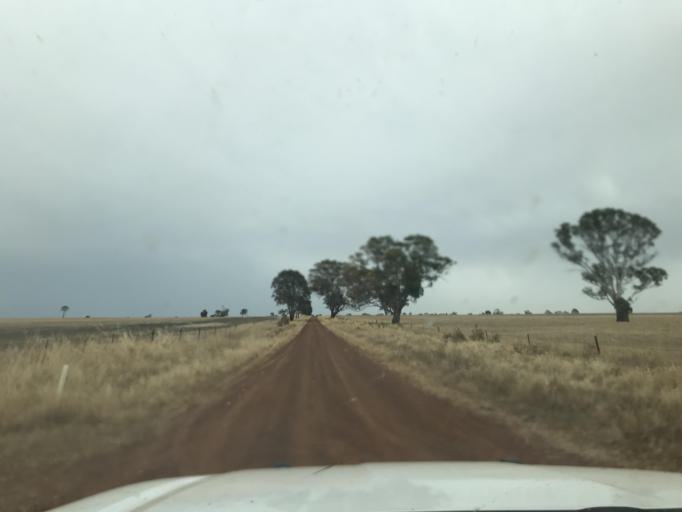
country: AU
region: Victoria
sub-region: Horsham
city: Horsham
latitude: -37.0644
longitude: 141.6502
